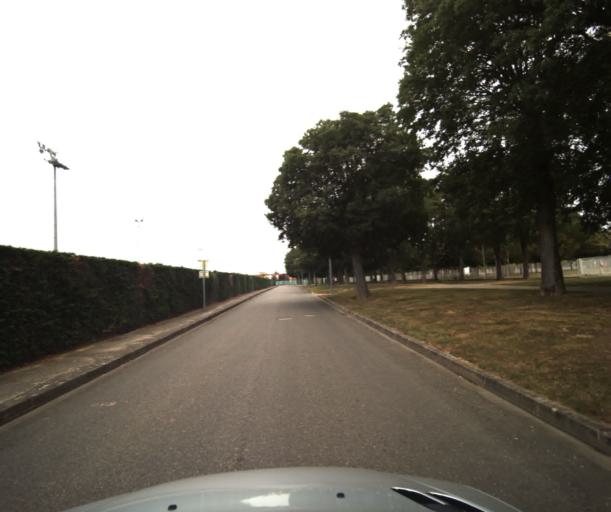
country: FR
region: Midi-Pyrenees
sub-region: Departement de la Haute-Garonne
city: Portet-sur-Garonne
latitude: 43.5300
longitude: 1.4128
